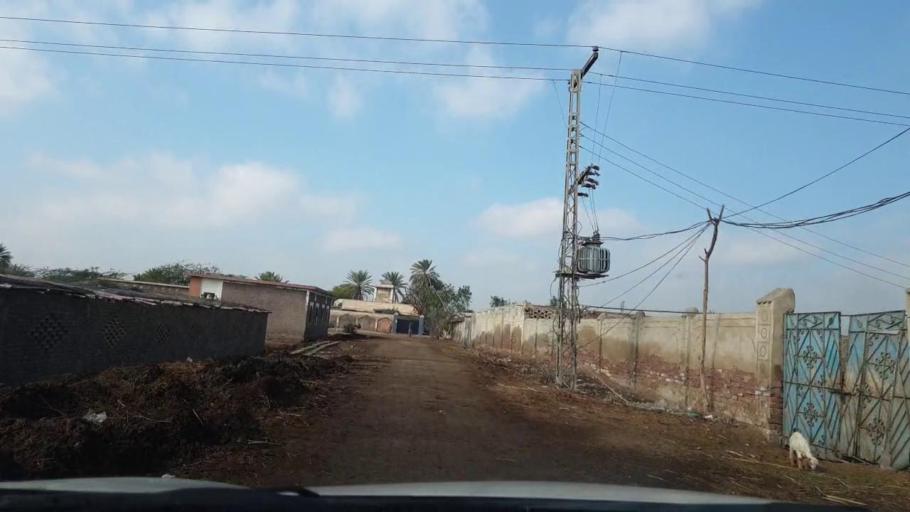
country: PK
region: Sindh
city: Mirpur Khas
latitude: 25.7705
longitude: 69.0710
